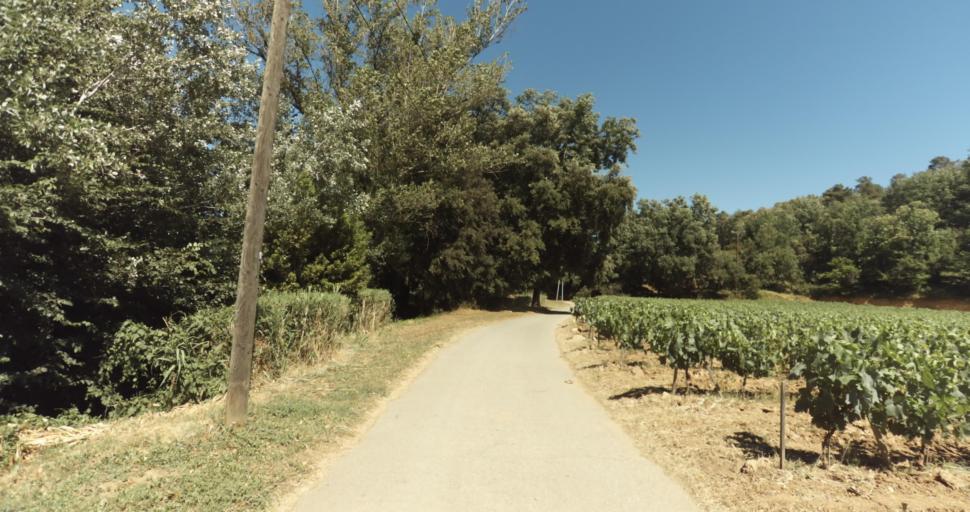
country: FR
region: Provence-Alpes-Cote d'Azur
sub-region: Departement du Var
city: Gassin
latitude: 43.2313
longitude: 6.5639
